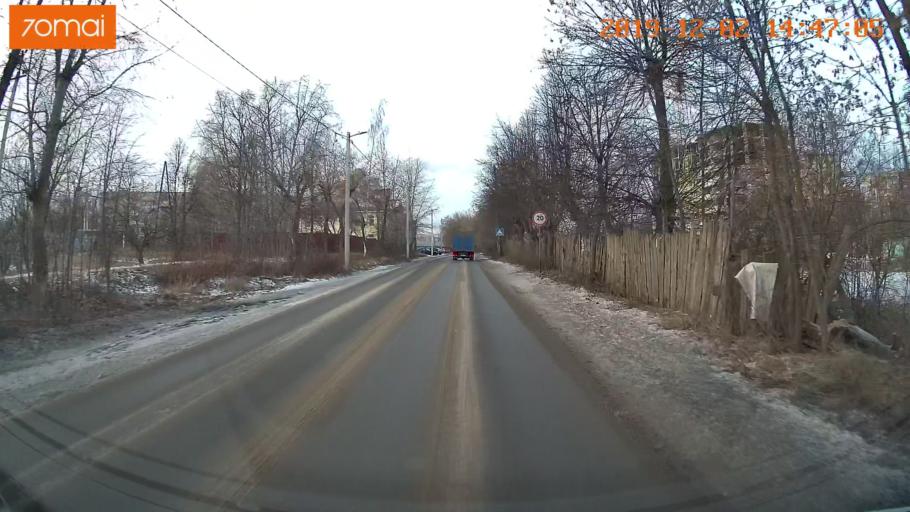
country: RU
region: Ivanovo
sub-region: Gorod Ivanovo
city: Ivanovo
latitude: 56.9876
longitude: 41.0220
